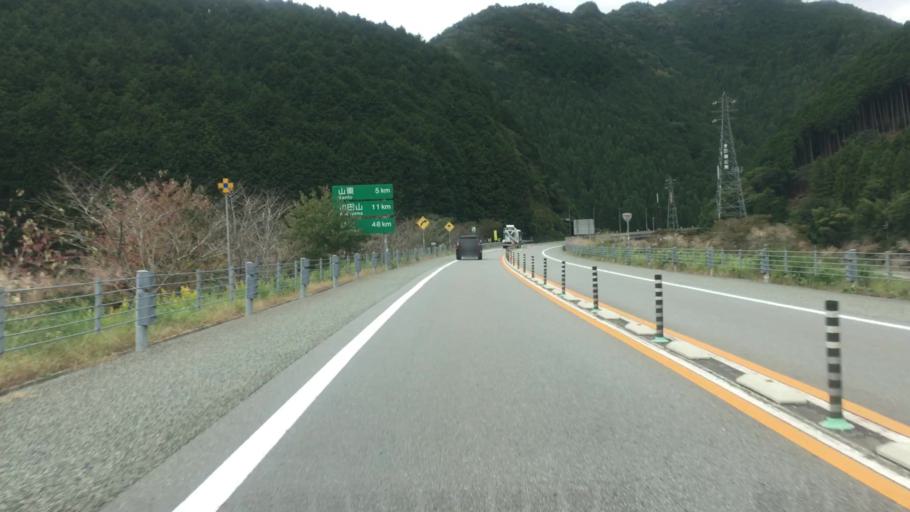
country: JP
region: Kyoto
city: Fukuchiyama
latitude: 35.2917
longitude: 134.9614
